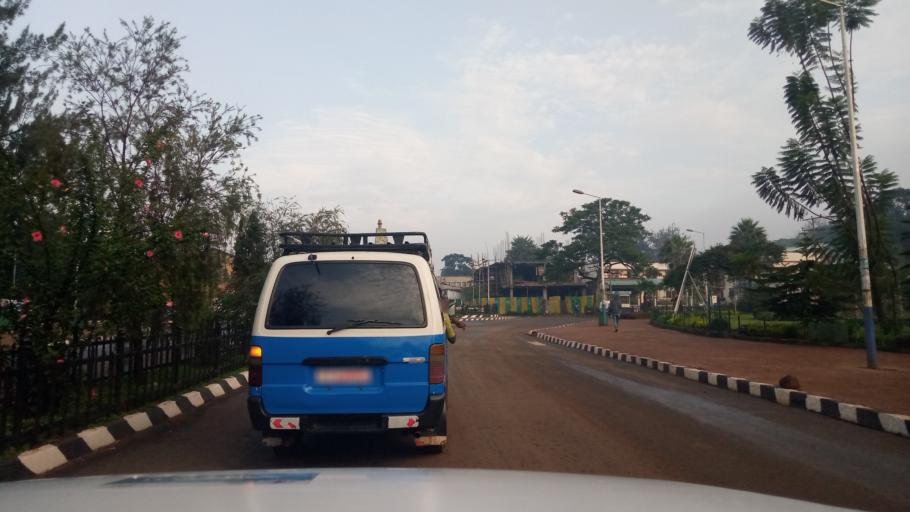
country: ET
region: Oromiya
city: Jima
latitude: 7.6760
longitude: 36.8350
